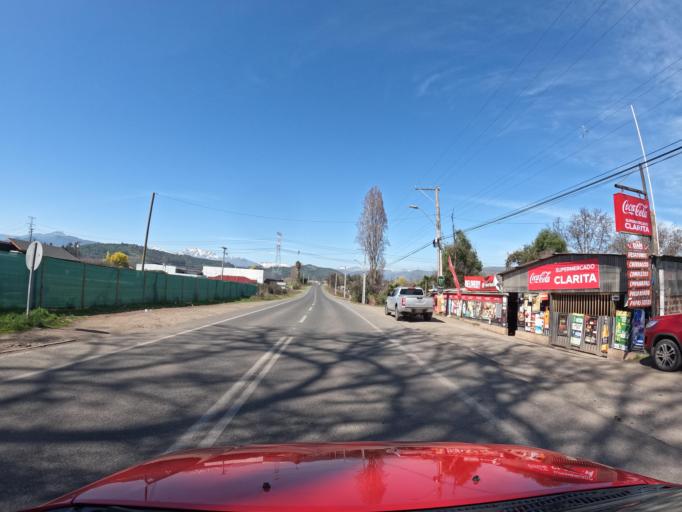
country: CL
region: Maule
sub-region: Provincia de Curico
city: Teno
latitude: -34.9696
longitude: -71.0091
